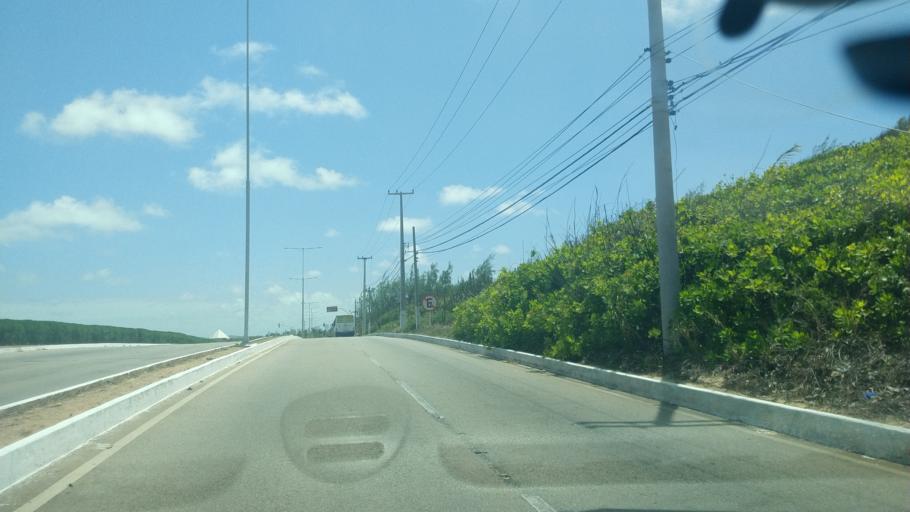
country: BR
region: Rio Grande do Norte
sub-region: Natal
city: Natal
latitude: -5.7983
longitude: -35.1827
